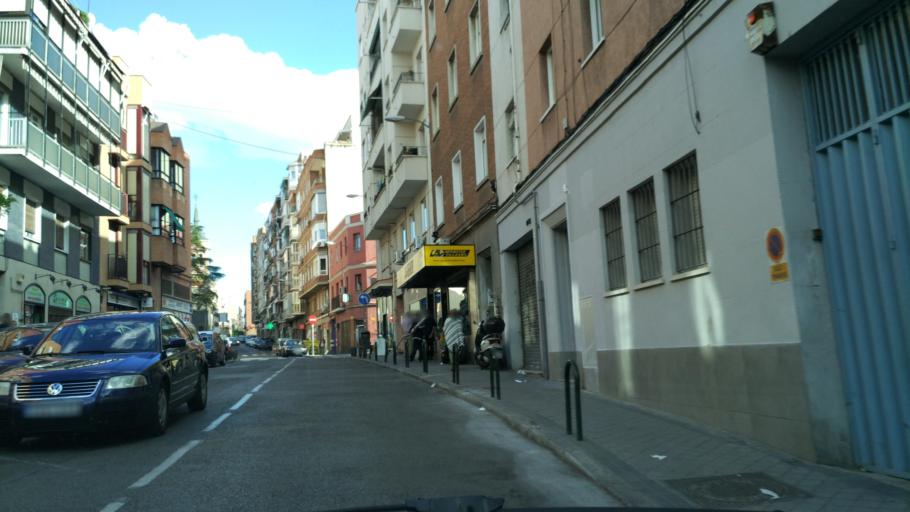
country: ES
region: Madrid
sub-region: Provincia de Madrid
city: Tetuan de las Victorias
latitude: 40.4591
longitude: -3.7074
